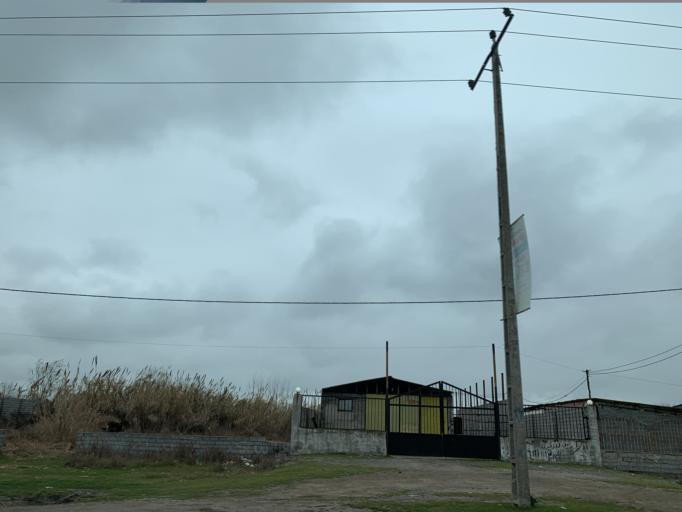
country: IR
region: Mazandaran
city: Babol
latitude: 36.5229
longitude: 52.6052
